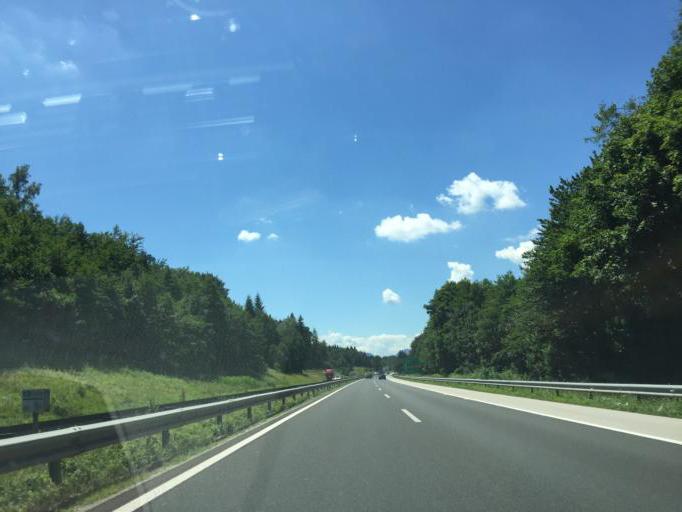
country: SI
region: Sentjur pri Celju
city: Sentjur
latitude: 46.2699
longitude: 15.4079
